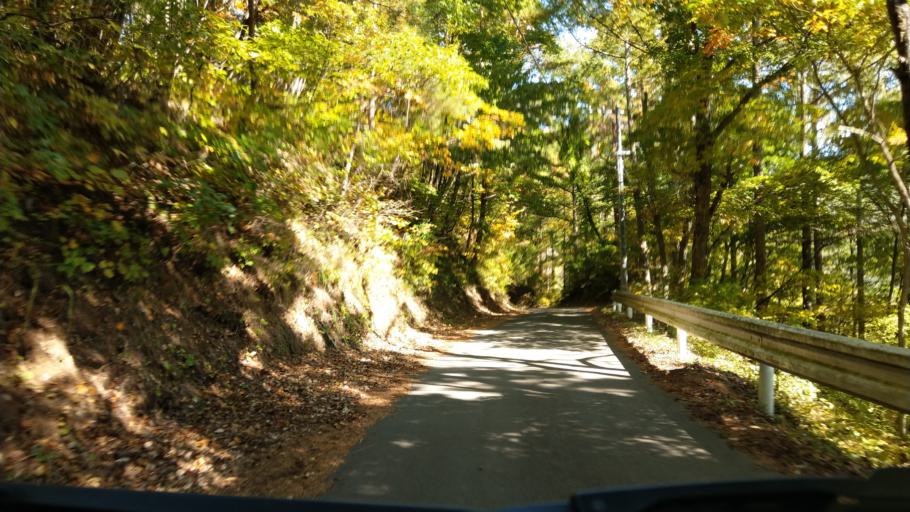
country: JP
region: Nagano
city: Komoro
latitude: 36.3692
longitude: 138.4096
